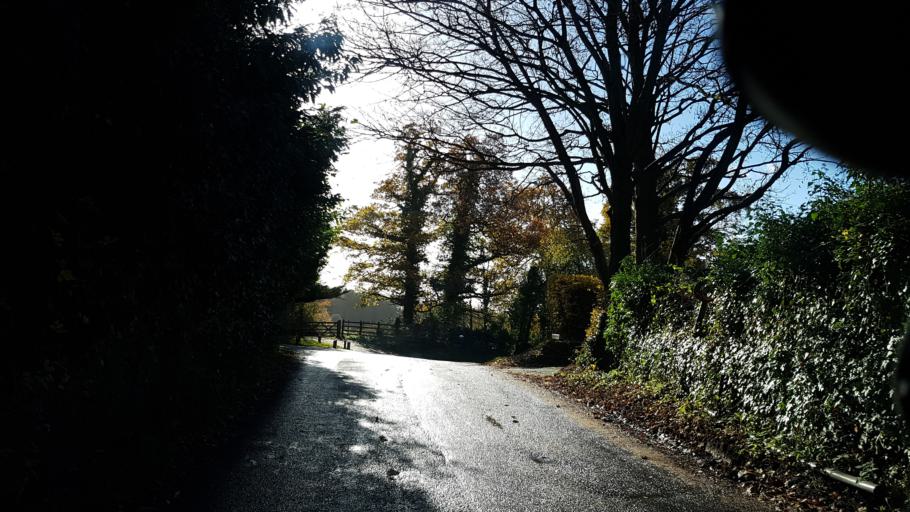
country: GB
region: England
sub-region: Surrey
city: Normandy
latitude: 51.2217
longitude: -0.6676
